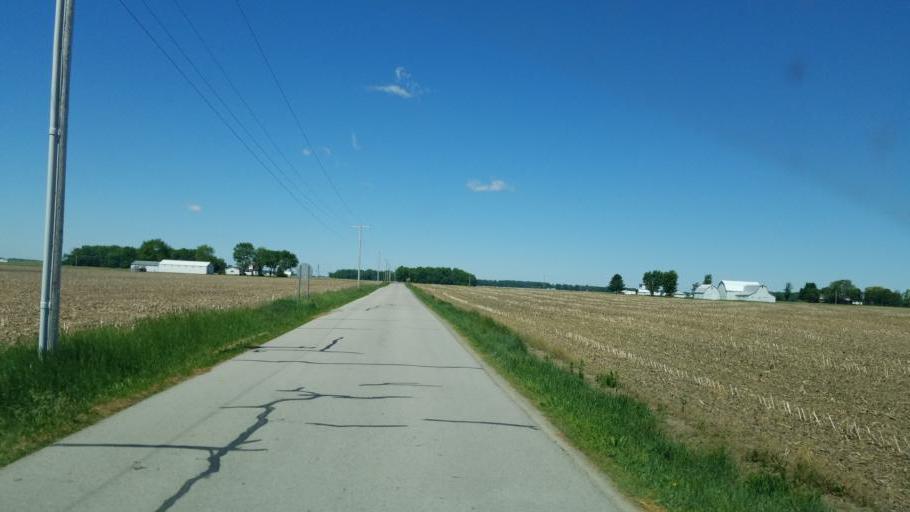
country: US
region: Ohio
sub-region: Shelby County
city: Jackson Center
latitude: 40.4181
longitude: -84.0351
